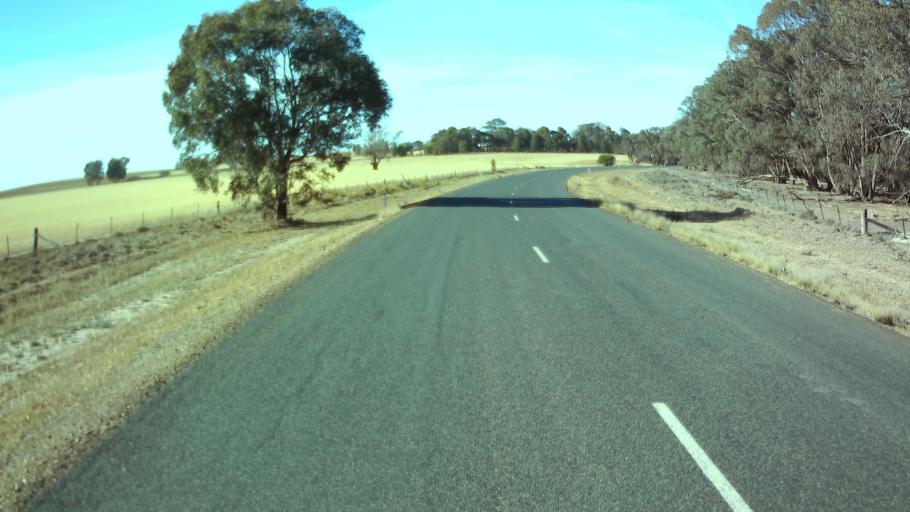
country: AU
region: New South Wales
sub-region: Weddin
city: Grenfell
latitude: -33.9860
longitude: 148.1407
